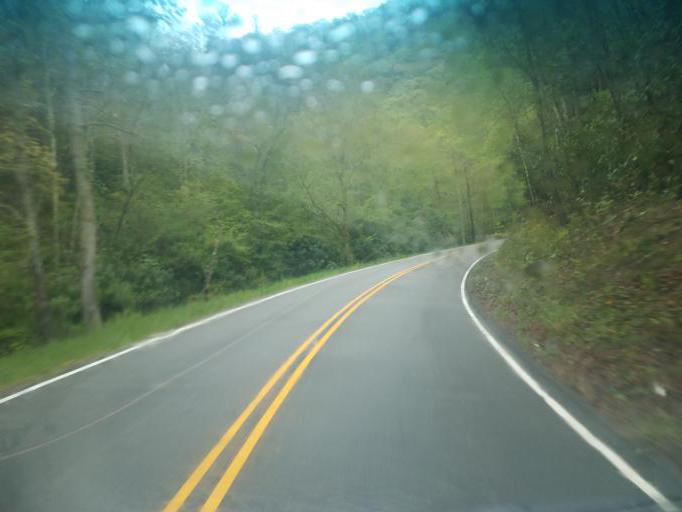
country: US
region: Virginia
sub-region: Washington County
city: Glade Spring
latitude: 36.6456
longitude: -81.7337
